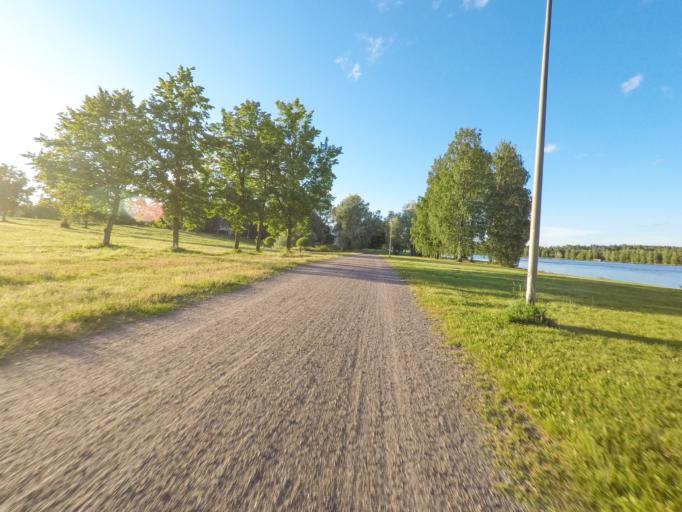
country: FI
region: South Karelia
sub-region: Imatra
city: Imatra
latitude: 61.1892
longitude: 28.7807
